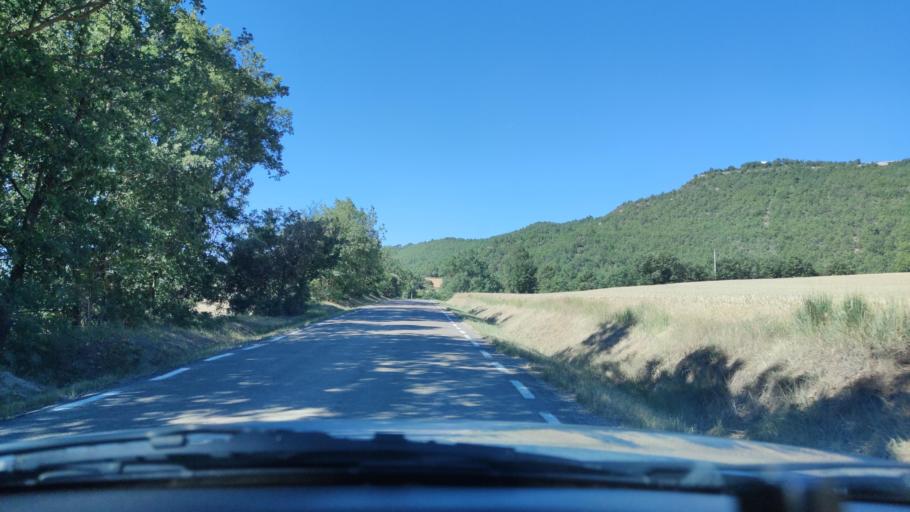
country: ES
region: Catalonia
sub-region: Provincia de Lleida
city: Solsona
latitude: 41.9701
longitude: 1.4985
